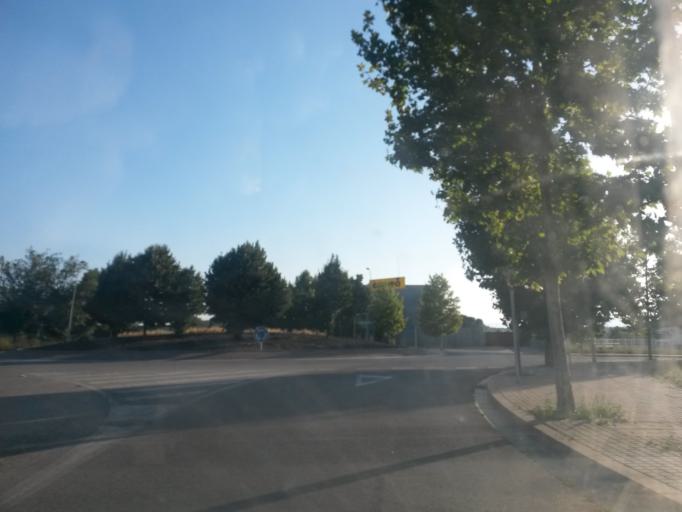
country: ES
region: Catalonia
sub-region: Provincia de Girona
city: Fornells de la Selva
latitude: 41.9461
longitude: 2.7991
